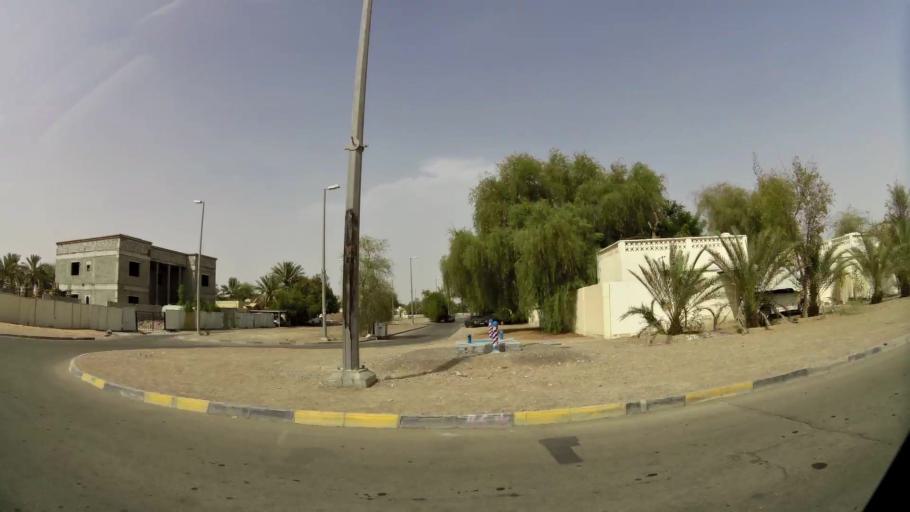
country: AE
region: Abu Dhabi
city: Al Ain
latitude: 24.1892
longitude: 55.6330
